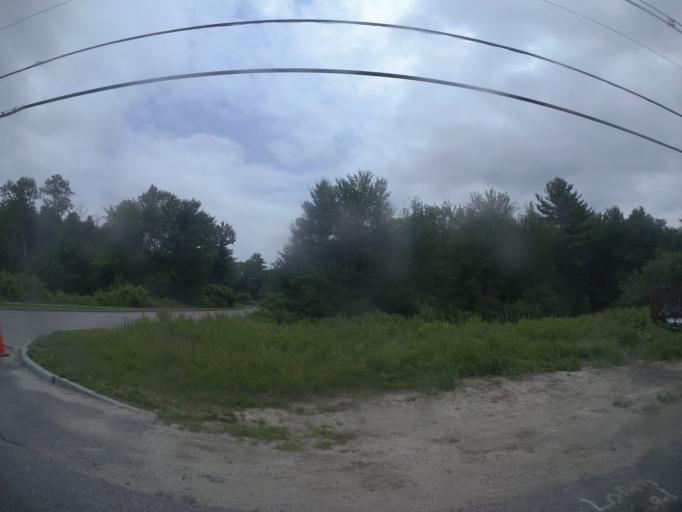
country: US
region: Maine
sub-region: Cumberland County
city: Cumberland Center
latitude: 43.7589
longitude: -70.2833
